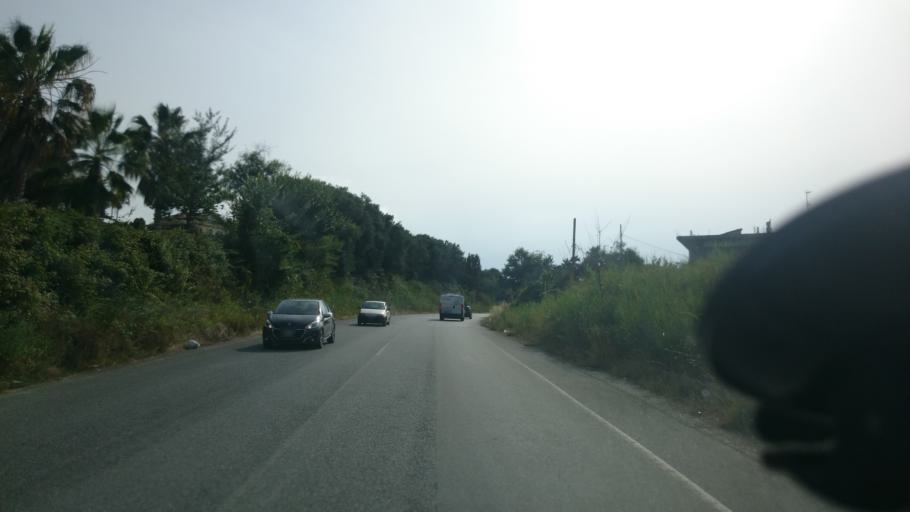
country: IT
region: Calabria
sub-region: Provincia di Vibo-Valentia
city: Vibo Valentia
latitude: 38.7071
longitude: 16.1023
